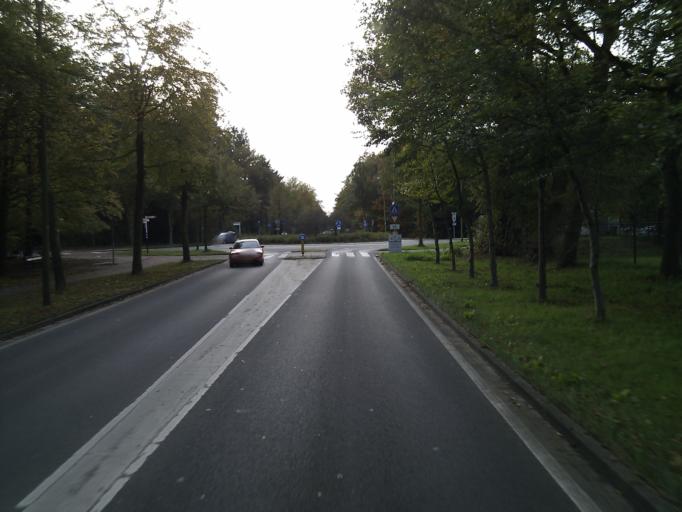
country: NL
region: Utrecht
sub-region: Gemeente Zeist
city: Zeist
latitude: 52.0846
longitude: 5.2537
